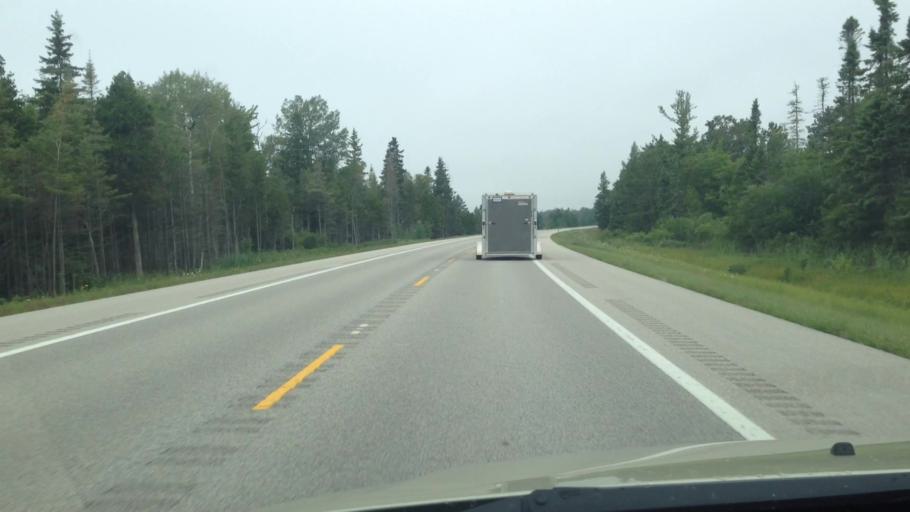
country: US
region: Michigan
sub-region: Luce County
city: Newberry
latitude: 46.0763
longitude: -85.2918
